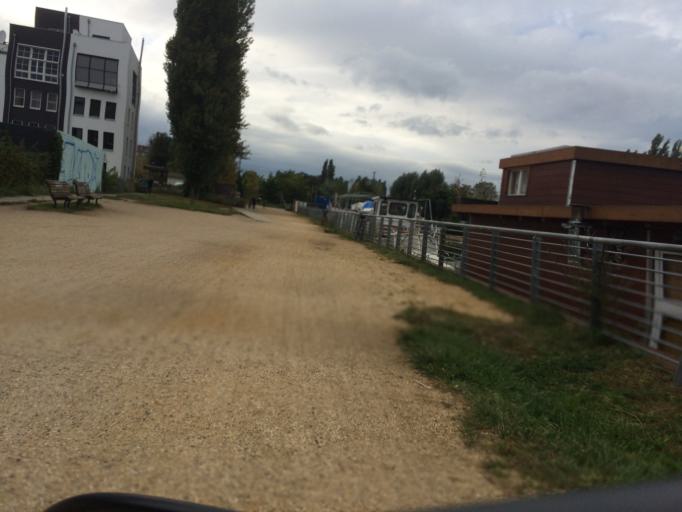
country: DE
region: Berlin
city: Treptow Bezirk
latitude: 52.4980
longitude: 13.4711
